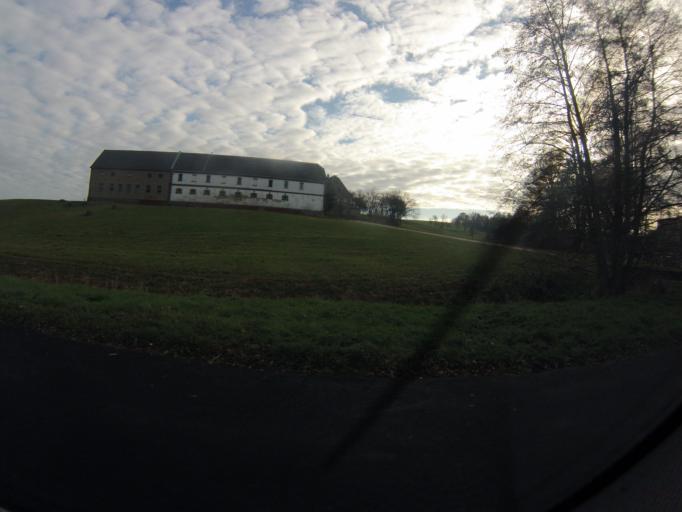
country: DE
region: Thuringia
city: Heyersdorf
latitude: 50.8534
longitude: 12.3606
